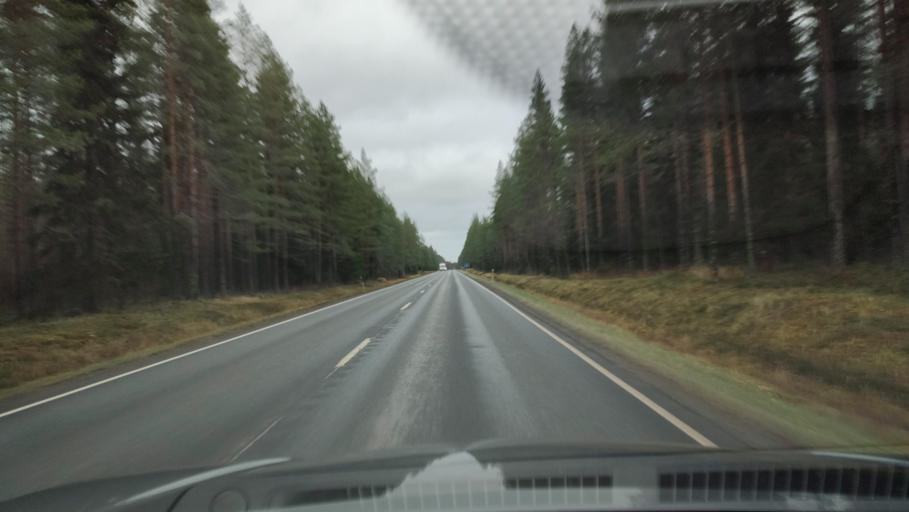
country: FI
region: Southern Ostrobothnia
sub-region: Seinaejoki
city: Kurikka
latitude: 62.5327
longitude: 22.3298
